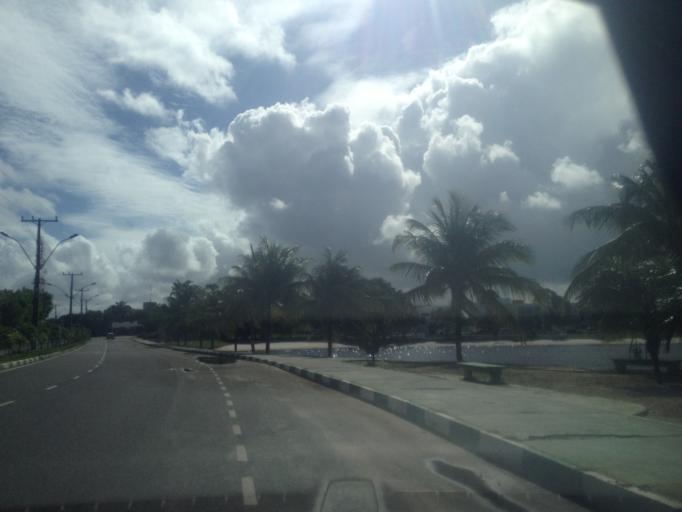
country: BR
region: Bahia
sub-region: Mata De Sao Joao
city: Mata de Sao Joao
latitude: -12.6479
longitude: -38.0740
